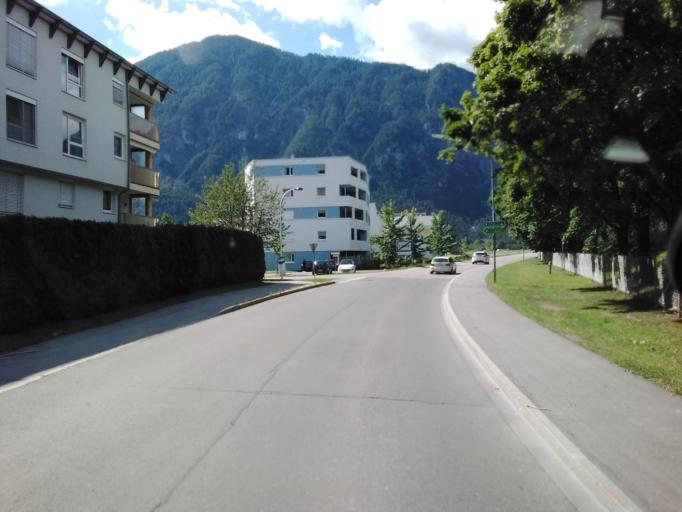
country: AT
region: Tyrol
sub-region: Politischer Bezirk Lienz
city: Lienz
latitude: 46.8245
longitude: 12.7684
